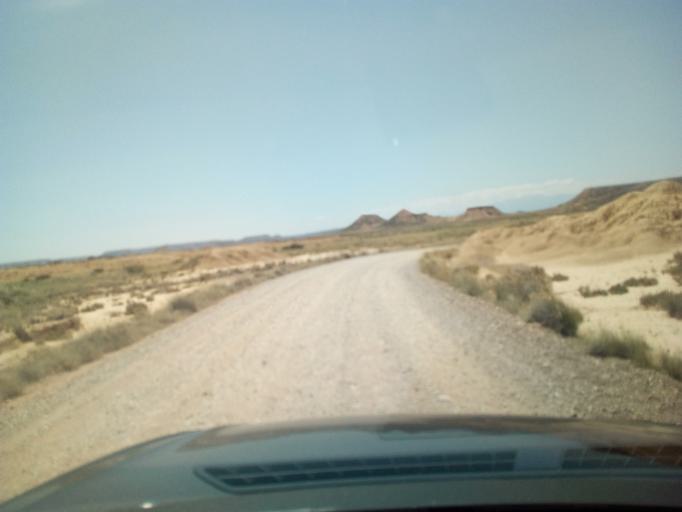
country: ES
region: Navarre
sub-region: Provincia de Navarra
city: Arguedas
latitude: 42.2259
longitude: -1.4924
